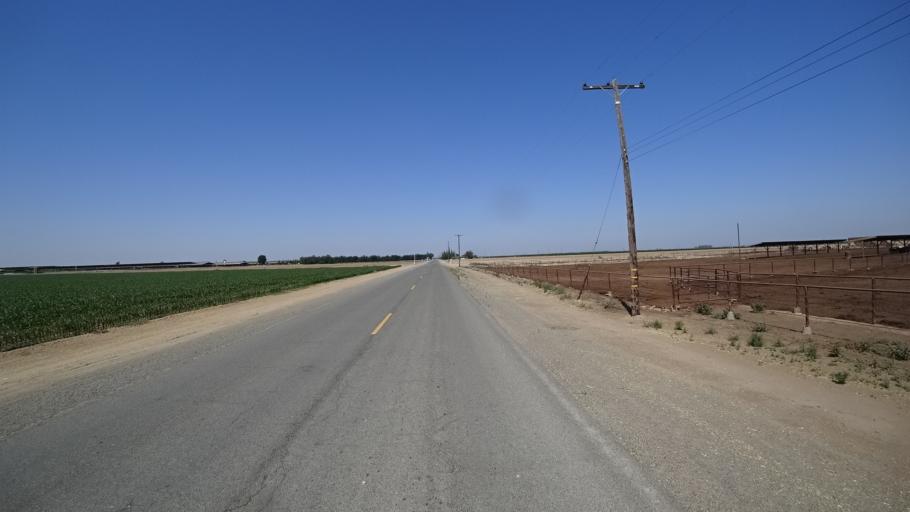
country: US
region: California
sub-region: Kings County
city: Hanford
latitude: 36.3720
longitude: -119.5674
